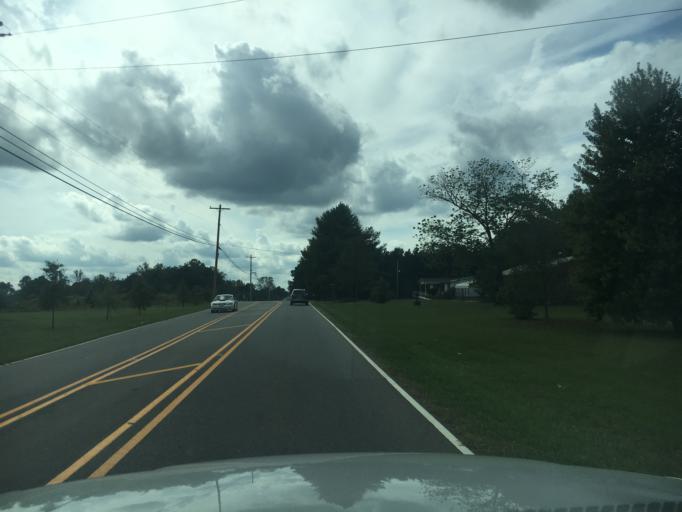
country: US
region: North Carolina
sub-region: Gaston County
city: Dallas
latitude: 35.3112
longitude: -81.2081
